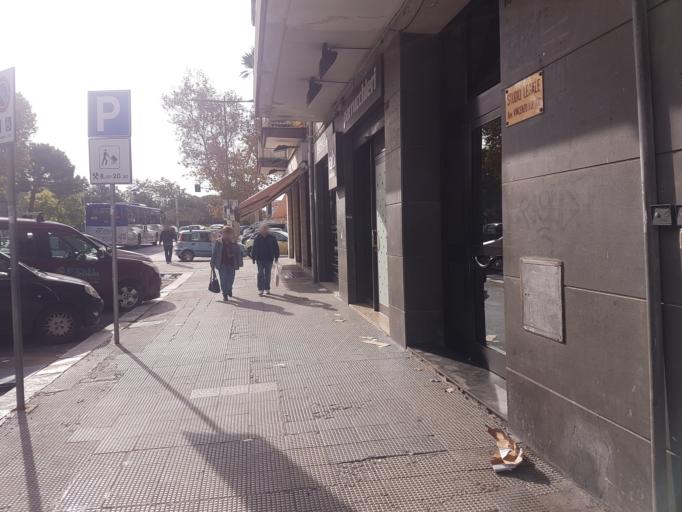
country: IT
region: Apulia
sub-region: Provincia di Bari
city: Bari
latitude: 41.1078
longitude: 16.8739
